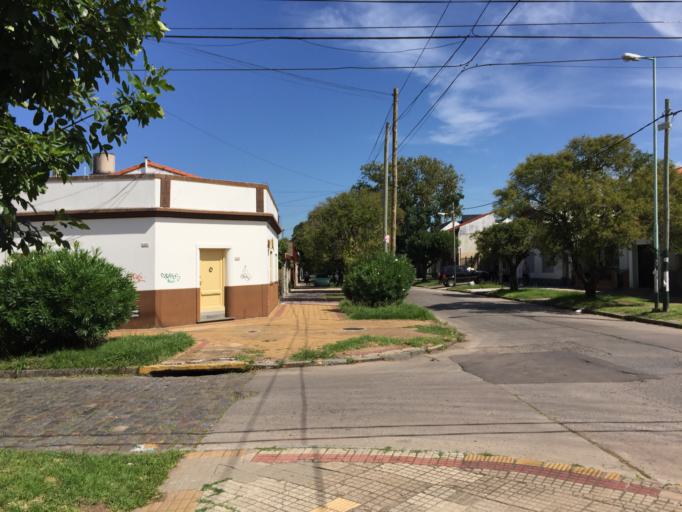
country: AR
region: Buenos Aires
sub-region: Partido de Lomas de Zamora
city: Lomas de Zamora
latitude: -34.7412
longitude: -58.3849
